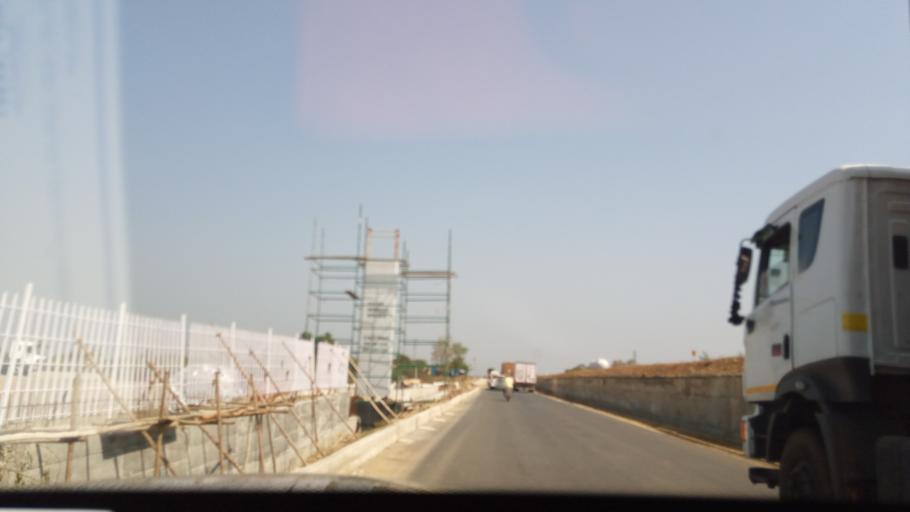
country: IN
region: Karnataka
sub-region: Dharwad
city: Hubli
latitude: 15.2501
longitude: 75.1452
